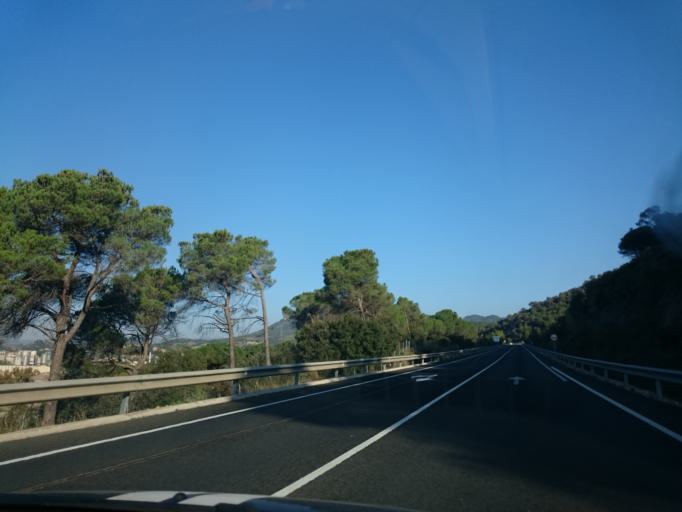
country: ES
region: Catalonia
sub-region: Provincia de Barcelona
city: Capellades
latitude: 41.5446
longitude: 1.6919
